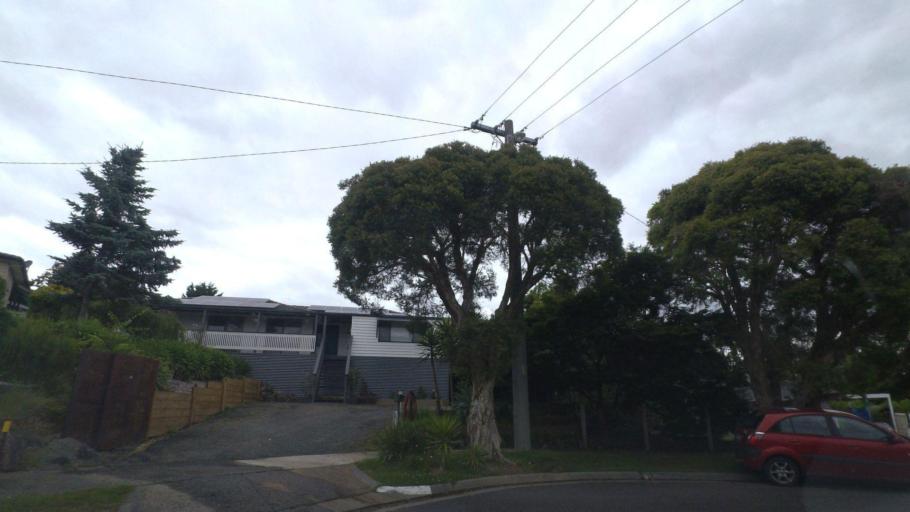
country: AU
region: Victoria
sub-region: Yarra Ranges
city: Mount Evelyn
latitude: -37.7754
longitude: 145.4272
